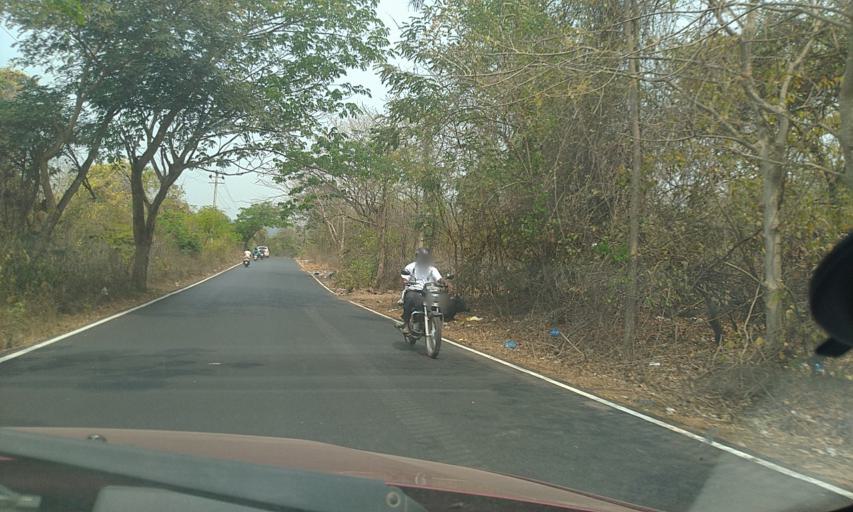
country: IN
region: Goa
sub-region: North Goa
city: Mapuca
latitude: 15.6100
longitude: 73.7965
